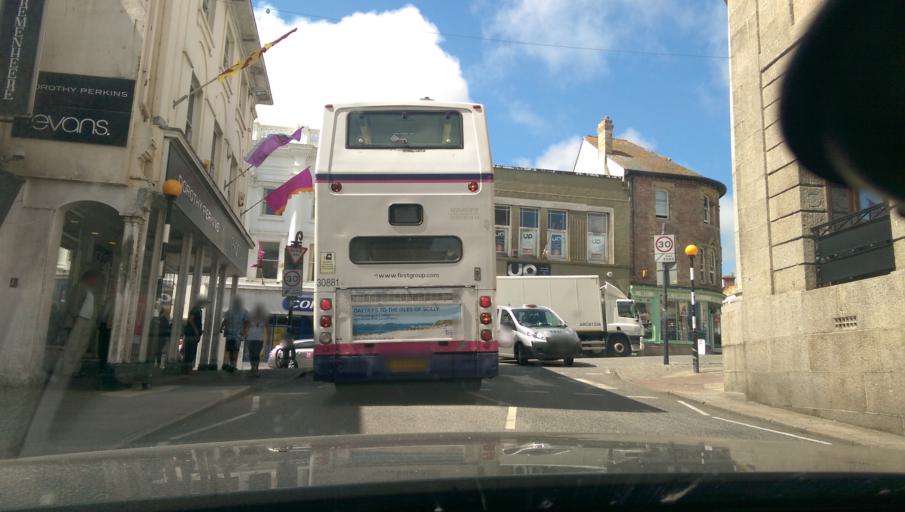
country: GB
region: England
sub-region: Cornwall
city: Penzance
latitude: 50.1187
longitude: -5.5368
